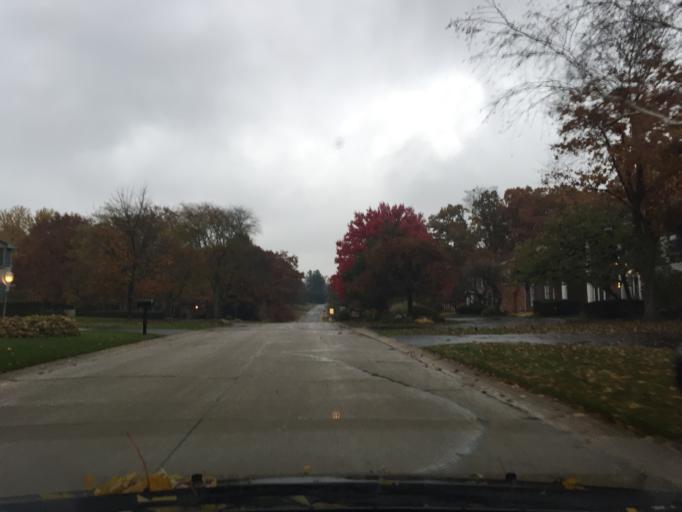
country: US
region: Michigan
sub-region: Oakland County
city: Bloomfield Hills
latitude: 42.5727
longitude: -83.2768
